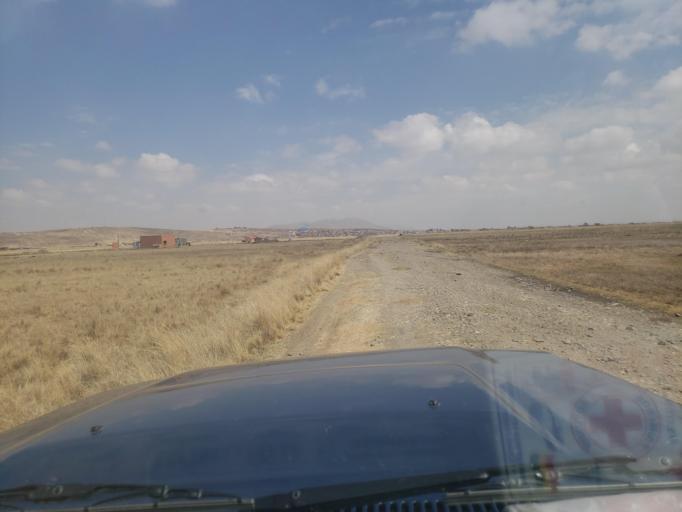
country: BO
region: La Paz
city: Batallas
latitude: -16.4058
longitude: -68.4555
